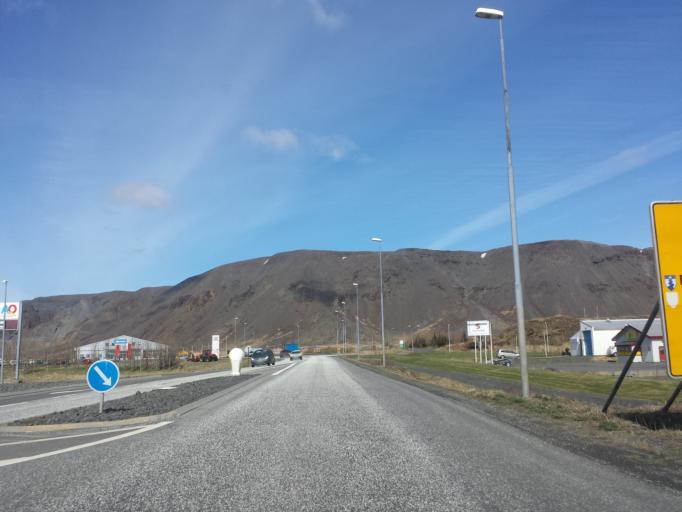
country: IS
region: South
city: Selfoss
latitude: 63.9465
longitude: -21.0119
